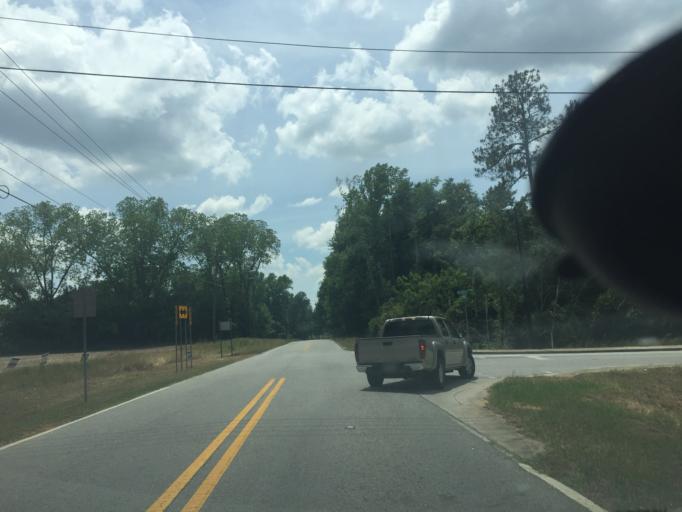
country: US
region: Georgia
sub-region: Bulloch County
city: Statesboro
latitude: 32.4280
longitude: -81.7521
